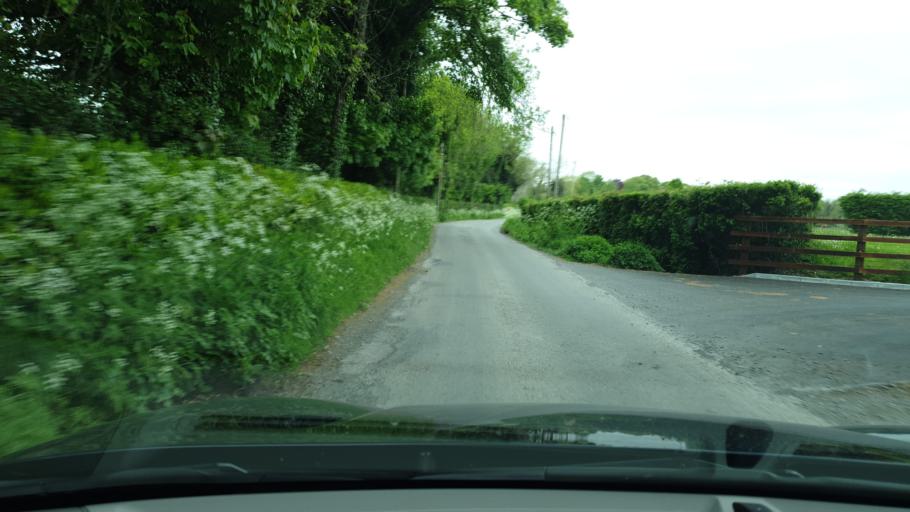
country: IE
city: Confey
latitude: 53.4386
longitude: -6.5255
